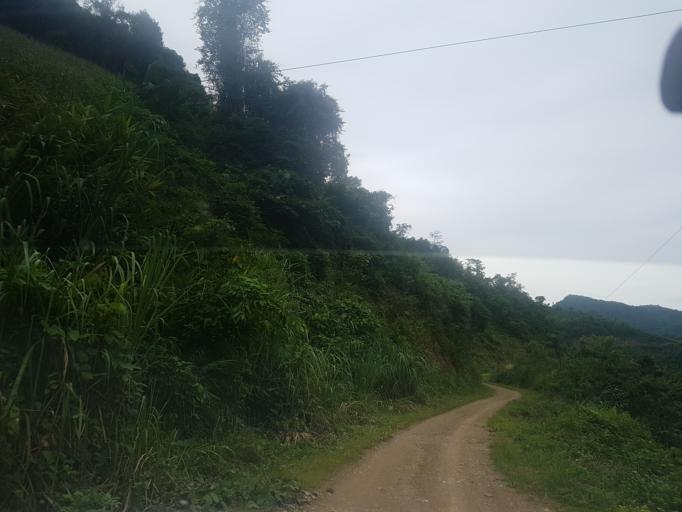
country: LA
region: Xiangkhoang
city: Phonsavan
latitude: 19.7460
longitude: 103.0712
